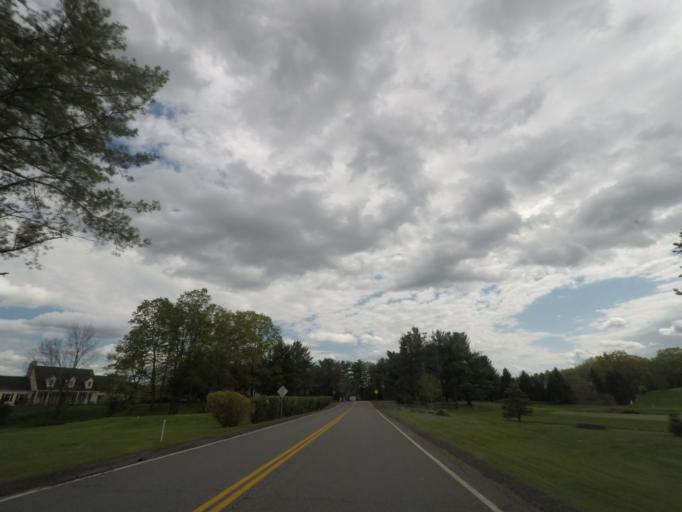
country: US
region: New York
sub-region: Albany County
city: Voorheesville
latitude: 42.6738
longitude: -73.9183
